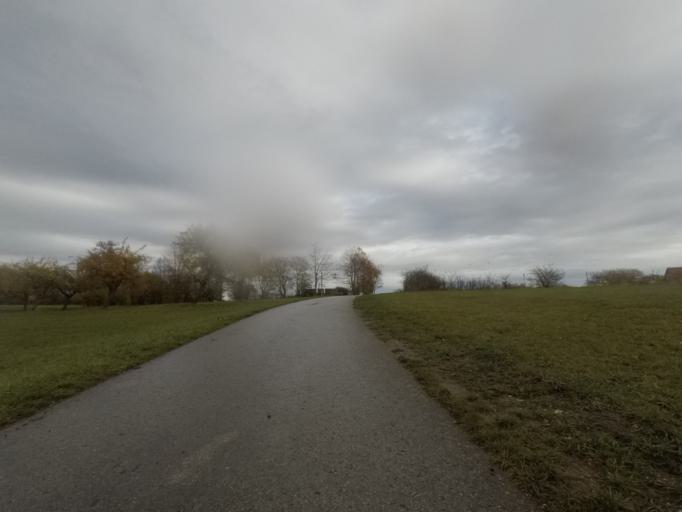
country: DE
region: Baden-Wuerttemberg
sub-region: Tuebingen Region
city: Sankt Johann
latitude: 48.4417
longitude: 9.3202
